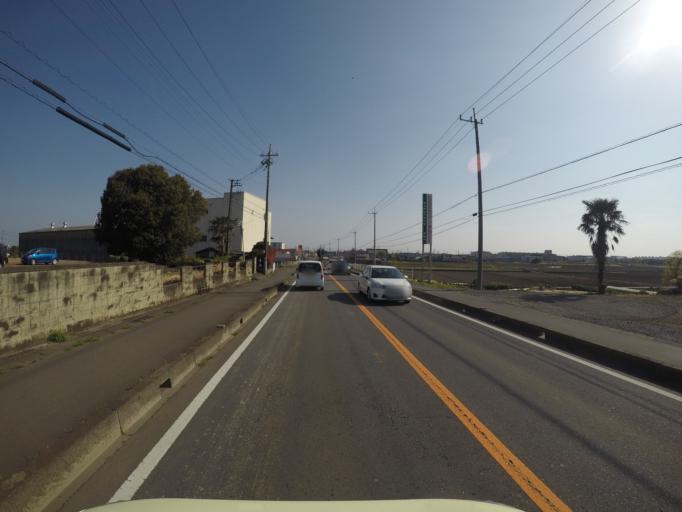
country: JP
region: Ibaraki
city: Yuki
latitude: 36.2766
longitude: 139.8788
